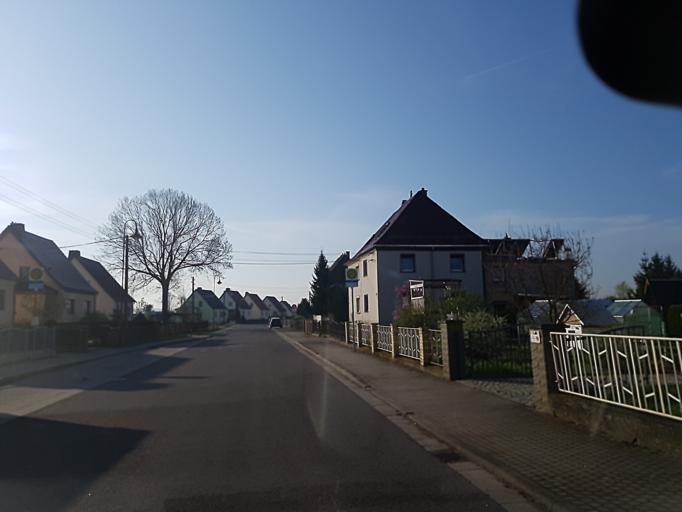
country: DE
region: Saxony
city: Mugeln
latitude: 51.2441
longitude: 13.0368
